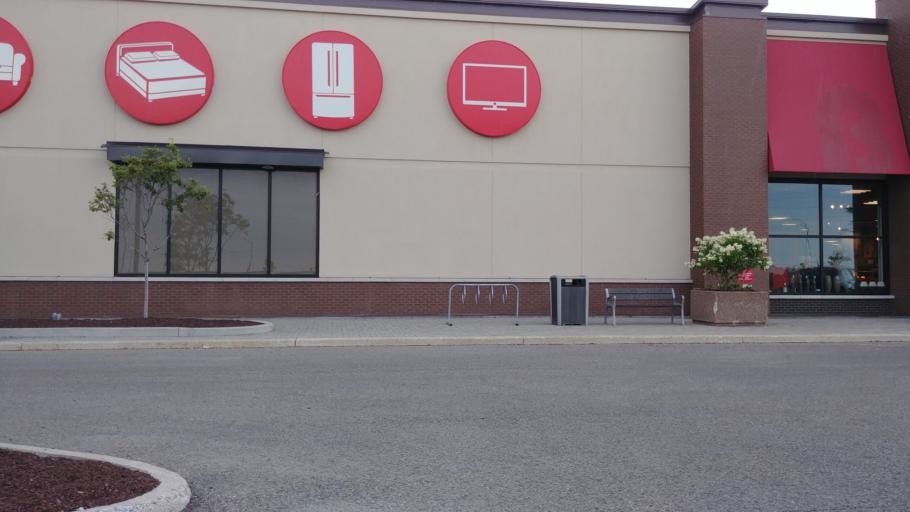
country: CA
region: Ontario
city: Bells Corners
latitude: 45.3049
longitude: -75.9223
